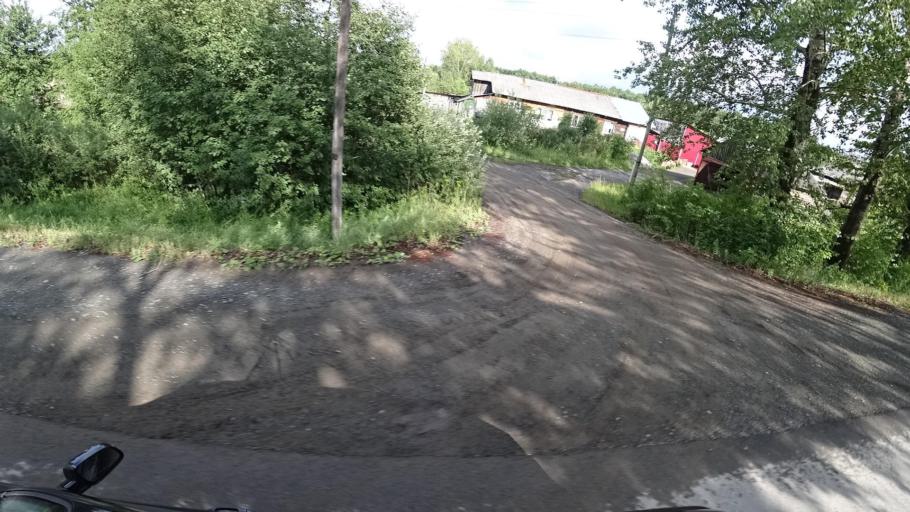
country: RU
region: Sverdlovsk
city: Kamyshlov
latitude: 56.8330
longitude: 62.6962
